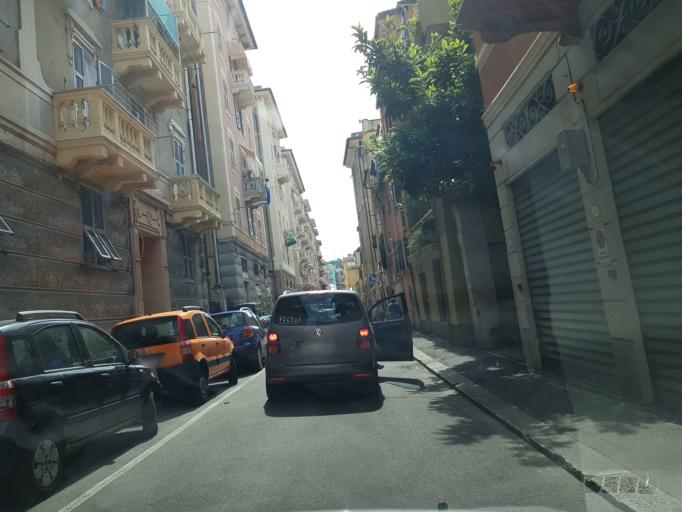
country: IT
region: Liguria
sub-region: Provincia di Genova
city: San Teodoro
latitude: 44.4264
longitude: 8.8472
